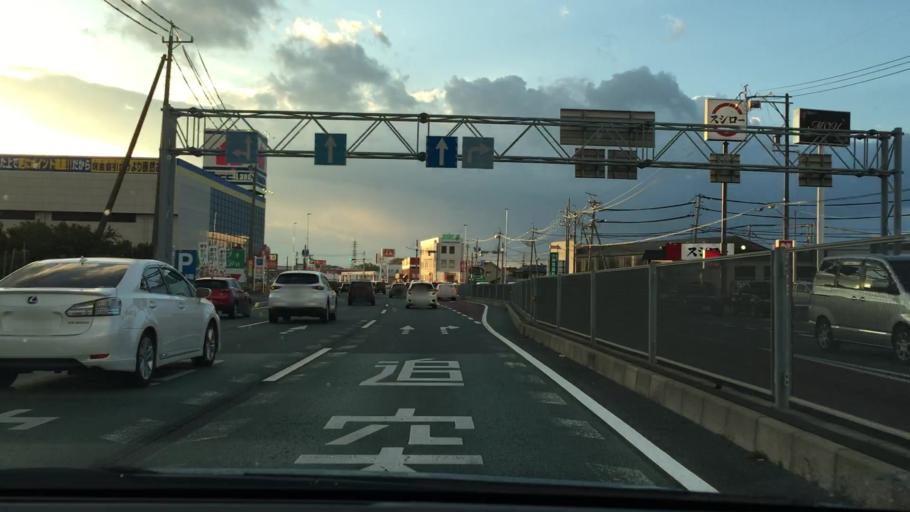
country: JP
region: Mie
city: Ise
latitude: 34.5086
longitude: 136.7227
